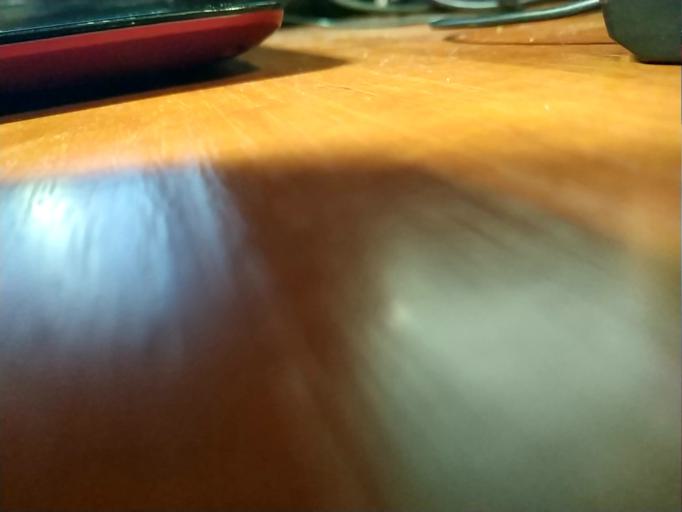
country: RU
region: Tverskaya
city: Likhoslavl'
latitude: 57.2204
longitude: 35.7137
